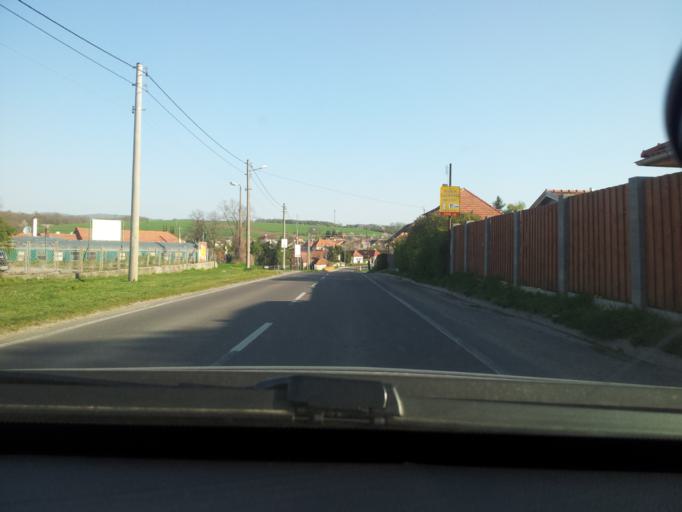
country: SK
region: Nitriansky
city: Zlate Moravce
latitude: 48.4127
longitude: 18.4087
